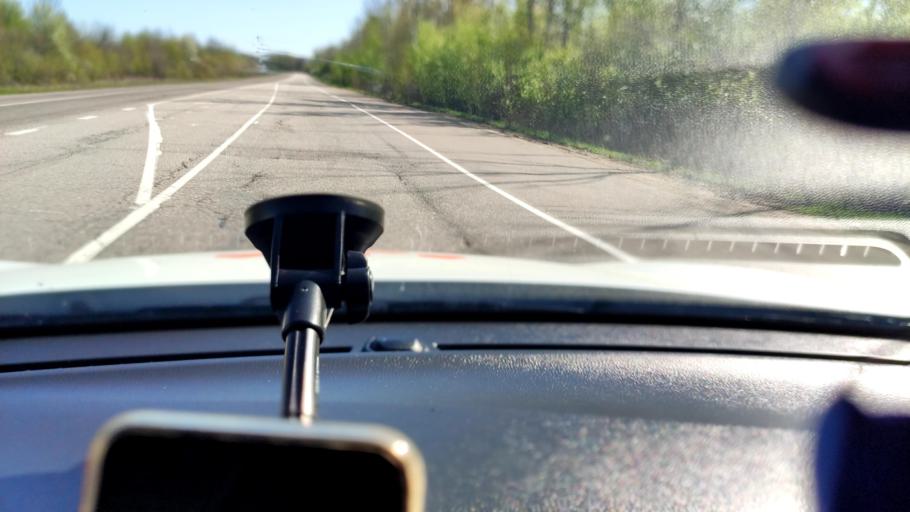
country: RU
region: Voronezj
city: Kolodeznyy
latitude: 51.2923
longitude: 39.0401
